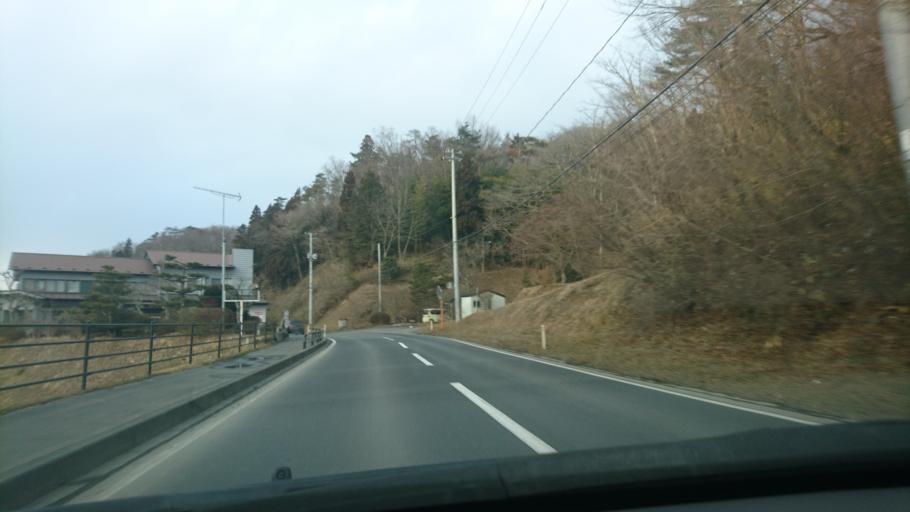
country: JP
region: Iwate
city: Ichinoseki
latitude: 38.9430
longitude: 141.3396
